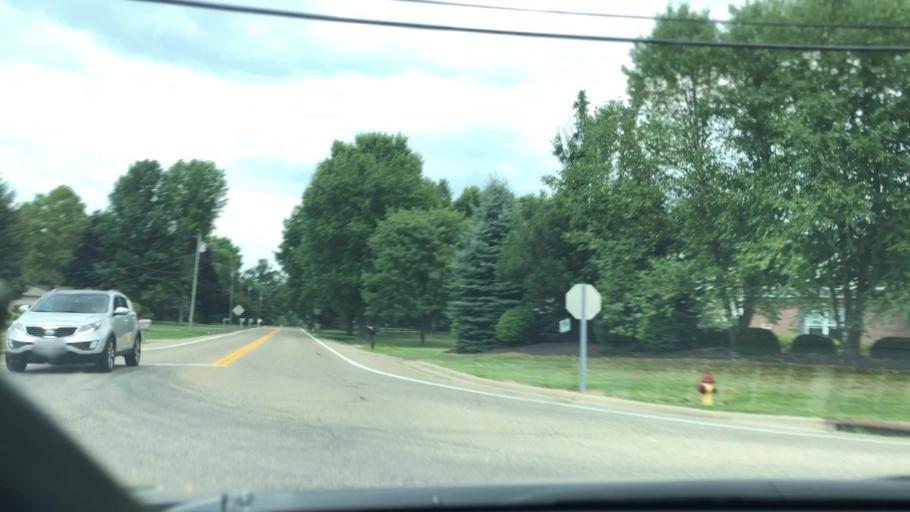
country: US
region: Ohio
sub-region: Summit County
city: New Franklin
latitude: 40.8948
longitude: -81.5179
